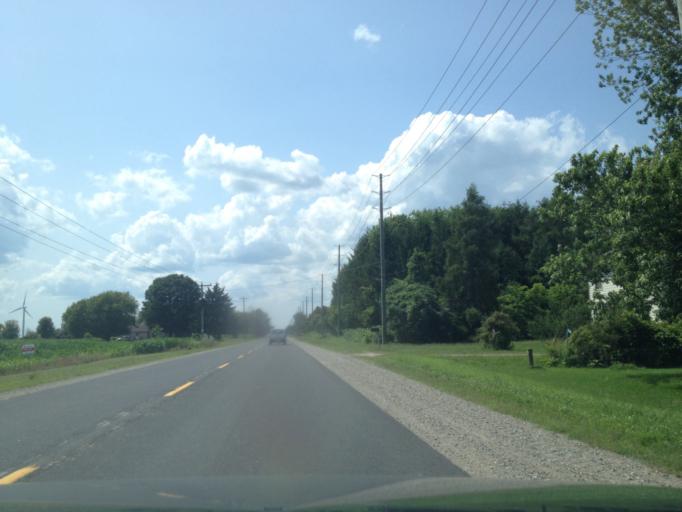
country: CA
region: Ontario
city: Aylmer
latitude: 42.6639
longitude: -80.8199
